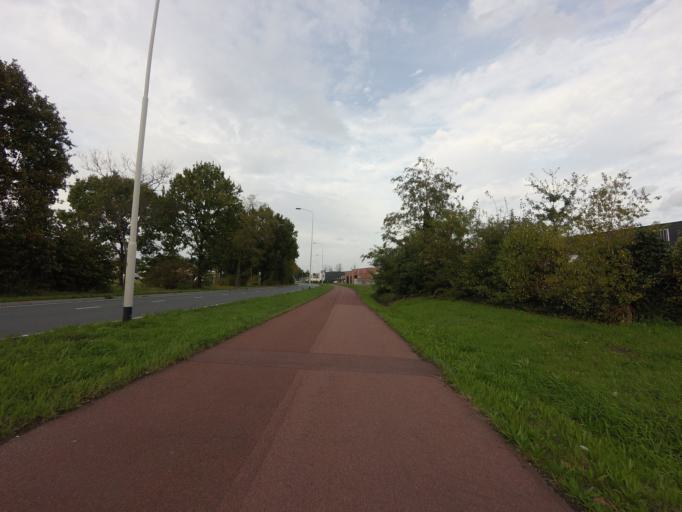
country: NL
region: North Brabant
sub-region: Gemeente Breda
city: Breda
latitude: 51.6095
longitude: 4.7535
